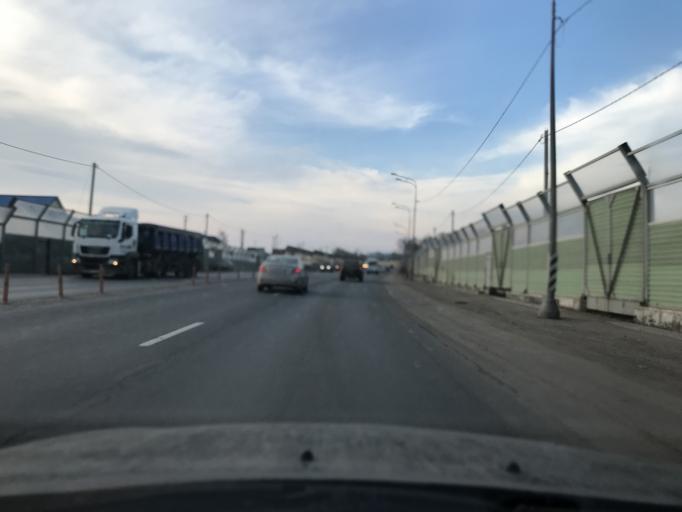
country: RU
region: Kaluga
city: Mstikhino
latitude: 54.5593
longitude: 36.1244
